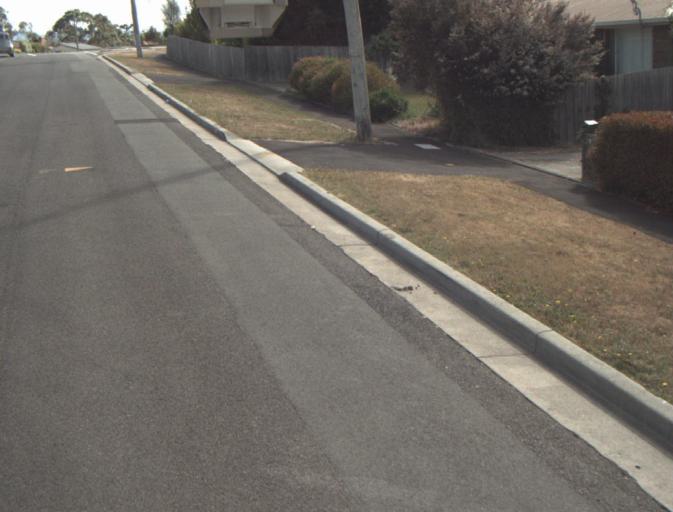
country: AU
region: Tasmania
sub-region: Launceston
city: Summerhill
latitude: -41.4664
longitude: 147.1158
